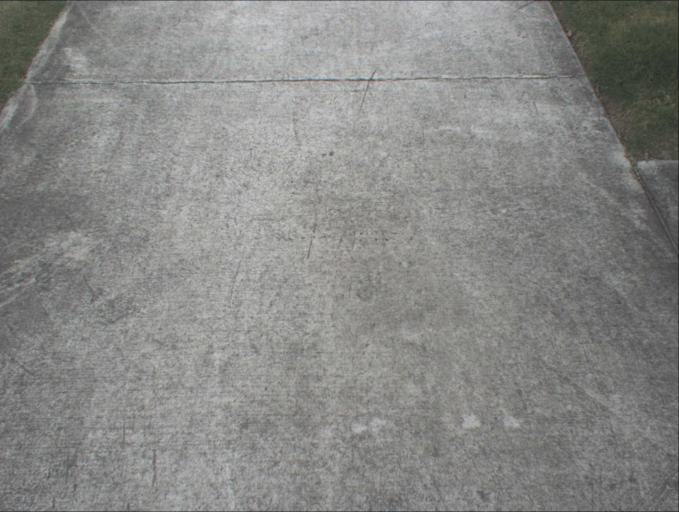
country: AU
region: Queensland
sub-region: Logan
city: Park Ridge South
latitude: -27.6921
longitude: 153.0343
